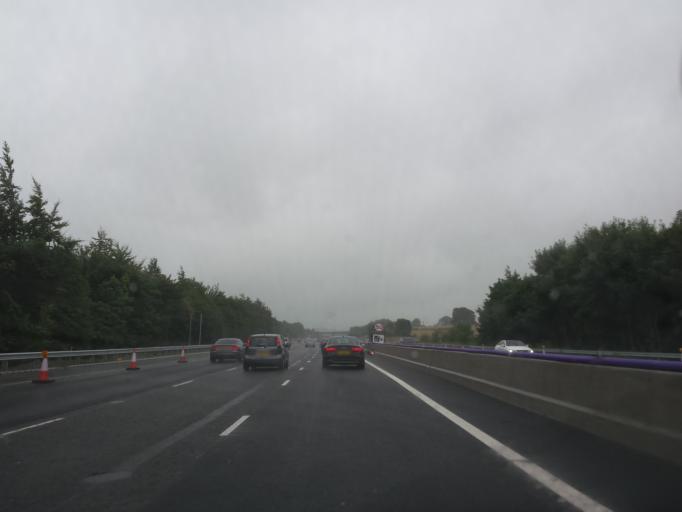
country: GB
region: England
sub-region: Derbyshire
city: Tibshelf
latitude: 53.1715
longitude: -1.3246
